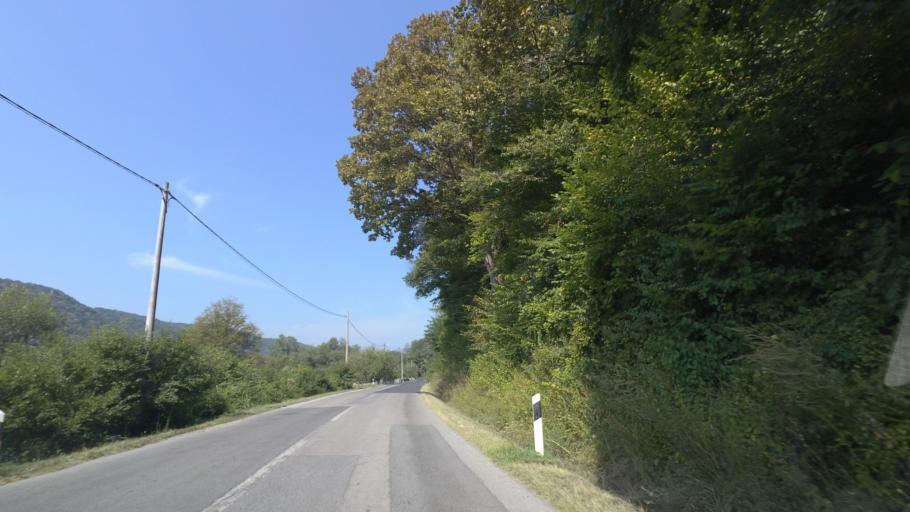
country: HR
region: Sisacko-Moslavacka
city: Dvor
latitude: 45.0728
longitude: 16.3633
